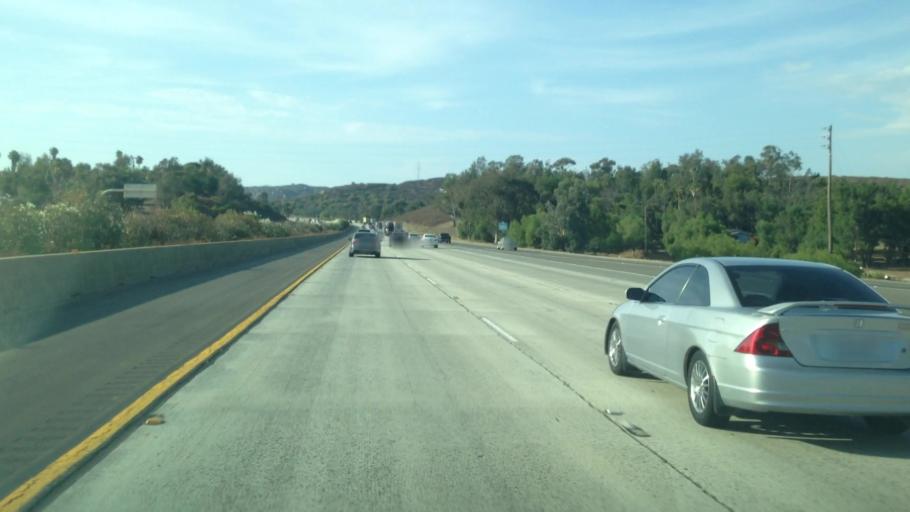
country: US
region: California
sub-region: San Diego County
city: Escondido
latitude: 33.1498
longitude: -117.1043
